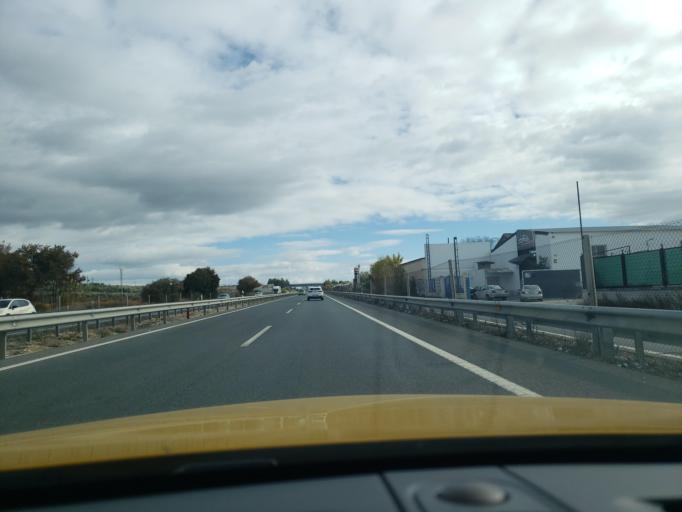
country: ES
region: Andalusia
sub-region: Provincia de Granada
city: Moraleda de Zafayona
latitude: 37.1835
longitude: -3.9544
